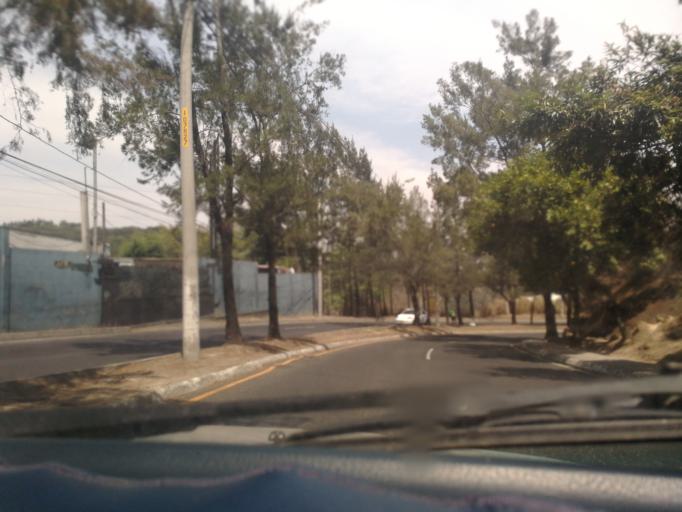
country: GT
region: Guatemala
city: Guatemala City
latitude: 14.6261
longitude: -90.4826
